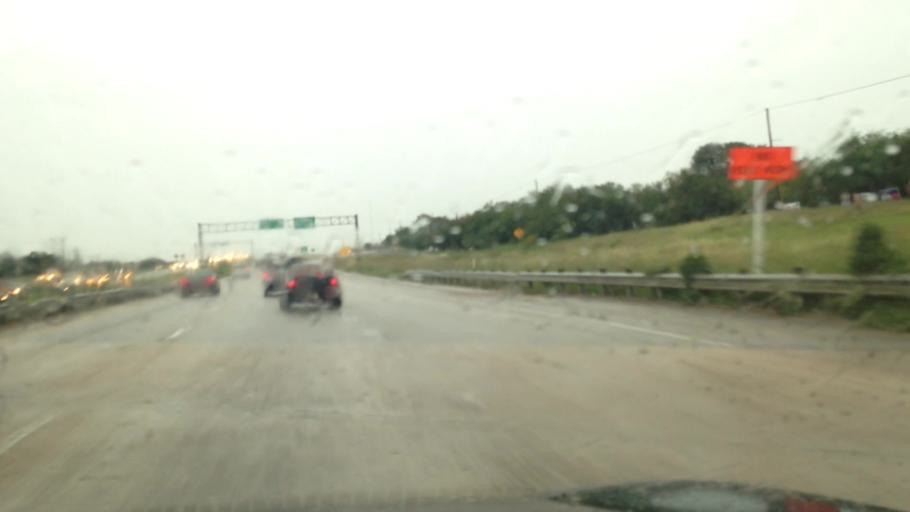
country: US
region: Texas
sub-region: Bexar County
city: Hollywood Park
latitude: 29.6010
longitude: -98.4123
